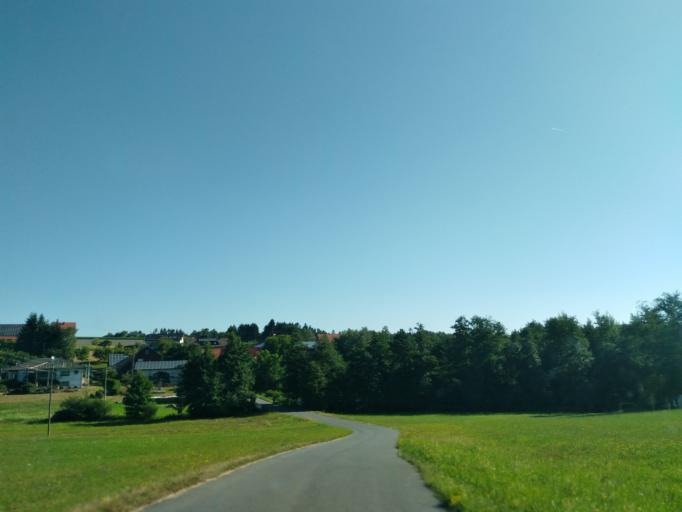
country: DE
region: Baden-Wuerttemberg
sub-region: Karlsruhe Region
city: Mudau
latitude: 49.5161
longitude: 9.1962
